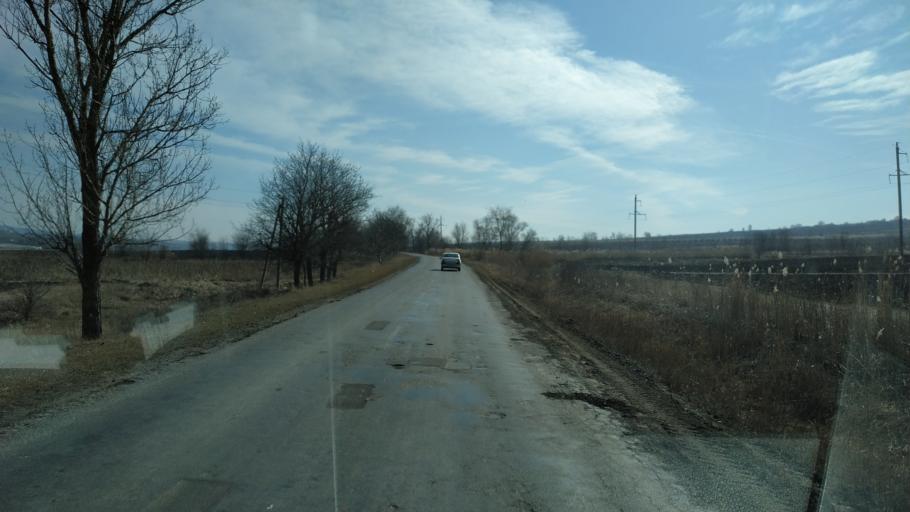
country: MD
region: Nisporeni
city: Nisporeni
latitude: 47.1047
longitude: 28.1262
